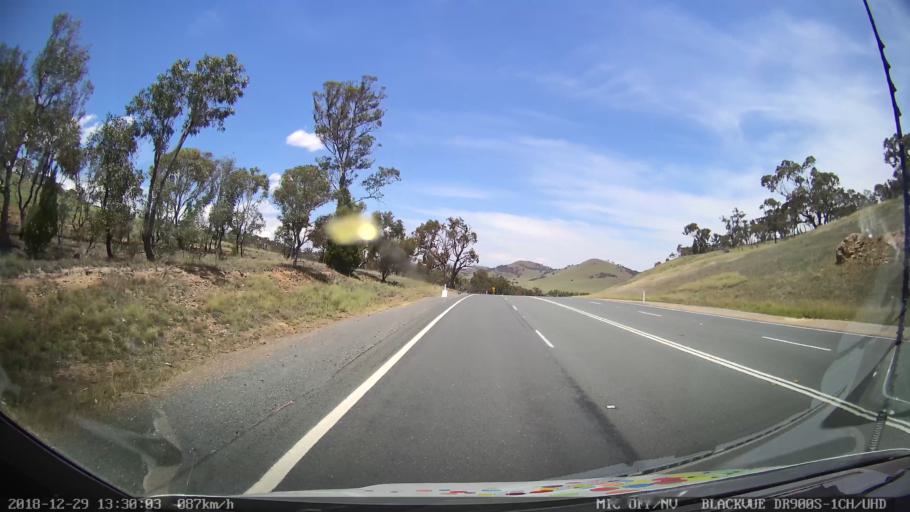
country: AU
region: New South Wales
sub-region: Cooma-Monaro
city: Cooma
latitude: -35.8985
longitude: 149.1614
